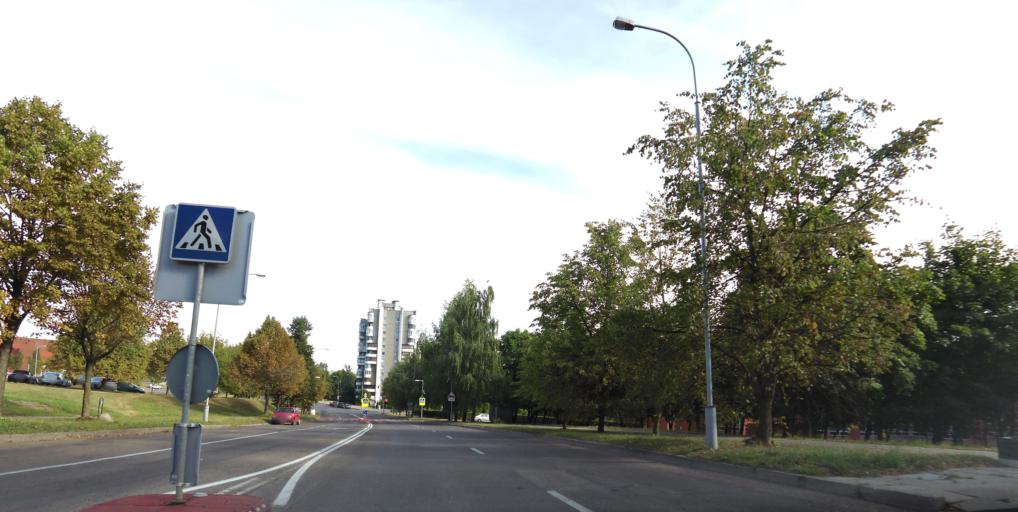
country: LT
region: Vilnius County
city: Seskine
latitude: 54.7144
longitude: 25.2517
